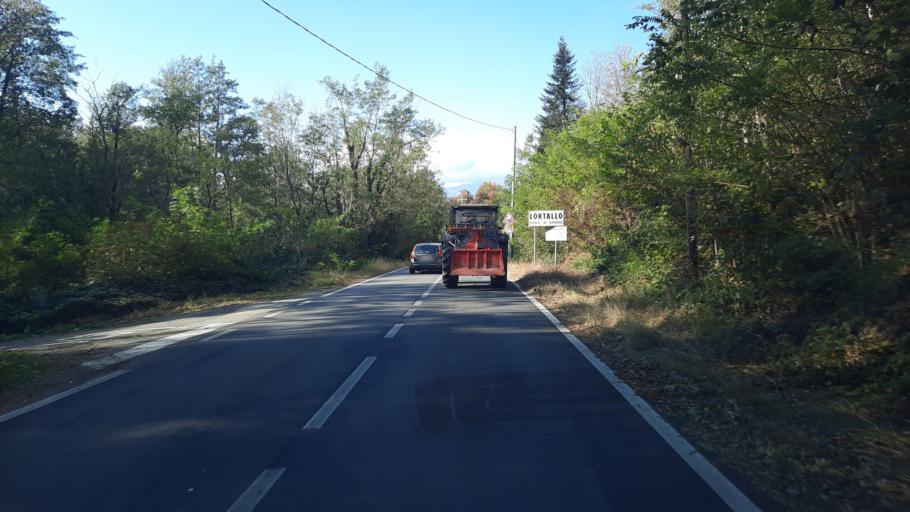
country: IT
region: Piedmont
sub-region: Provincia di Novara
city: Ameno
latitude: 45.7783
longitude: 8.4365
